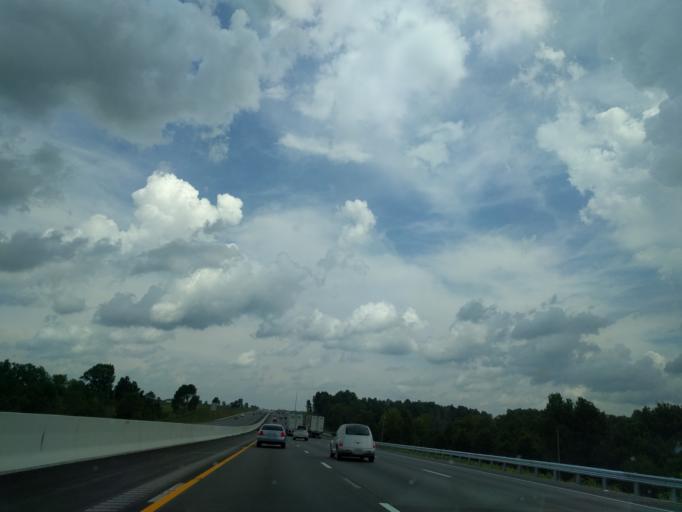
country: US
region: Kentucky
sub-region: Larue County
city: Hodgenville
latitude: 37.4753
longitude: -85.8817
